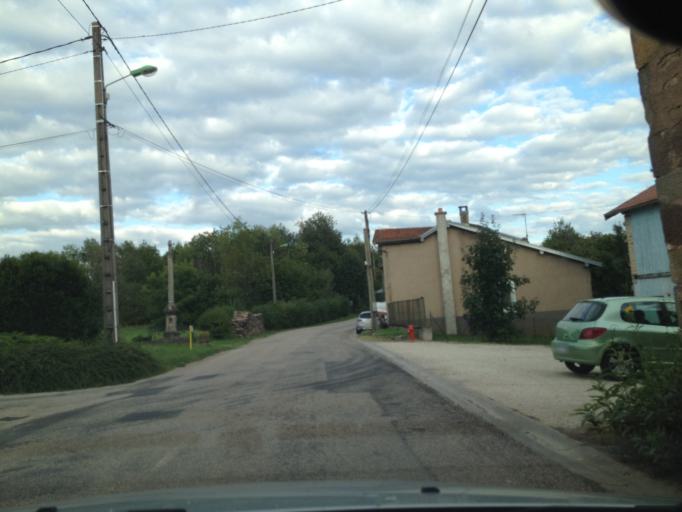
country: FR
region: Lorraine
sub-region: Departement des Vosges
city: Bains-les-Bains
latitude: 47.9734
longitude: 6.1767
